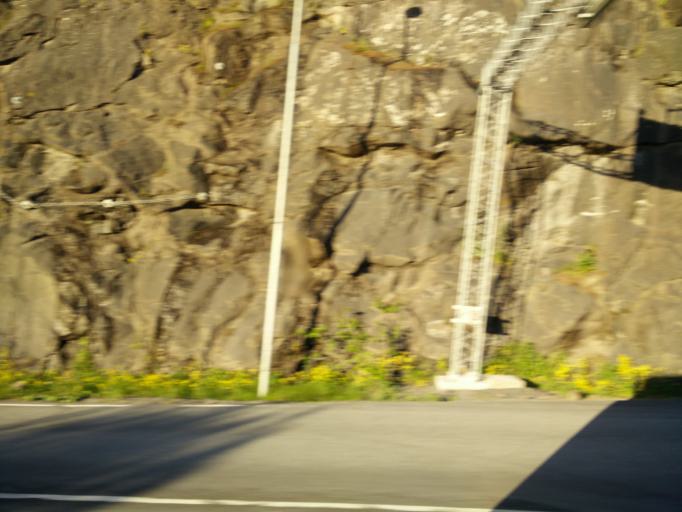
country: NO
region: Buskerud
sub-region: Hole
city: Vik
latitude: 59.9915
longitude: 10.3017
